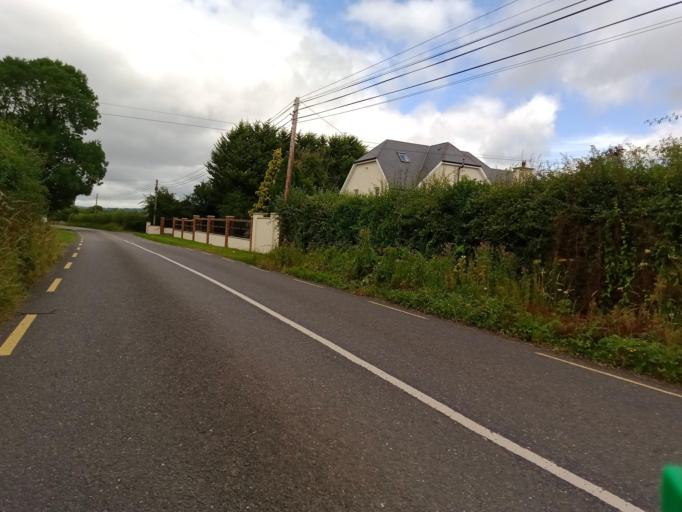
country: IE
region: Leinster
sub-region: Kilkenny
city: Callan
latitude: 52.5578
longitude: -7.4095
